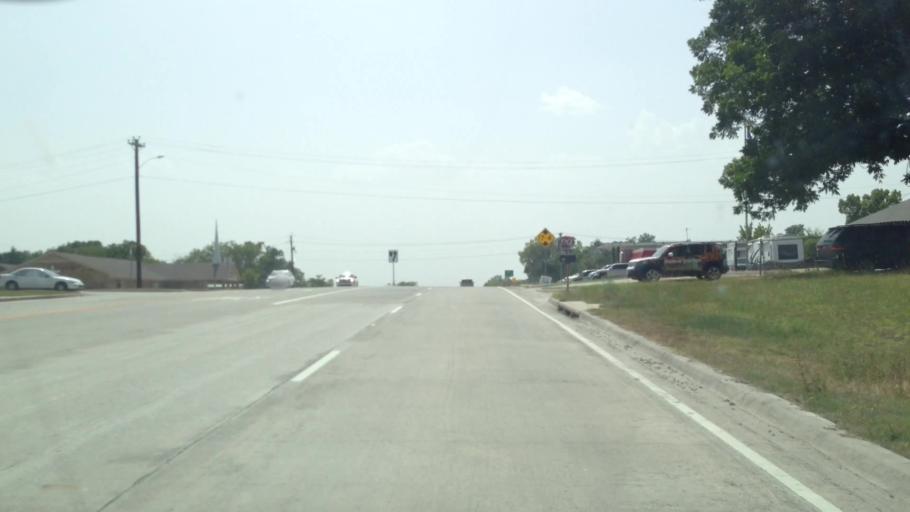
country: US
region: Texas
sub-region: Collin County
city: Farmersville
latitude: 33.1566
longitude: -96.3564
